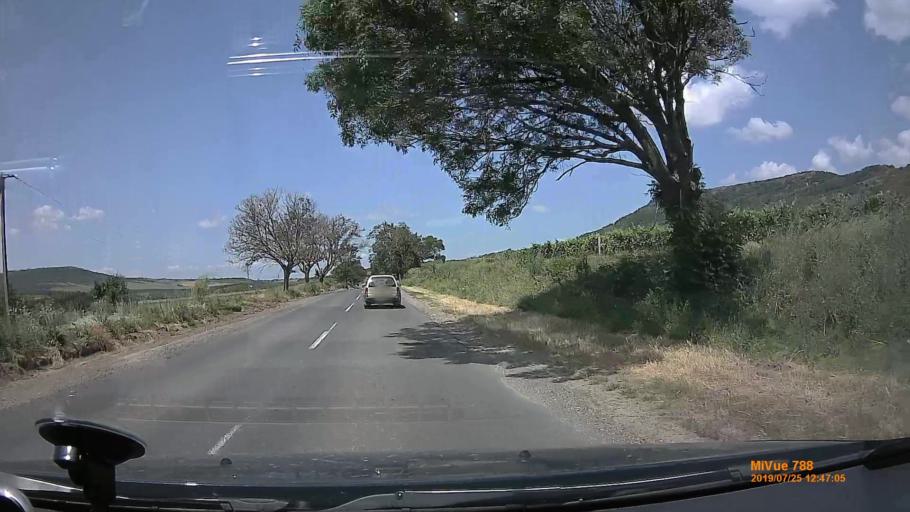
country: HU
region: Borsod-Abauj-Zemplen
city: Abaujszanto
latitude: 48.2557
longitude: 21.1928
